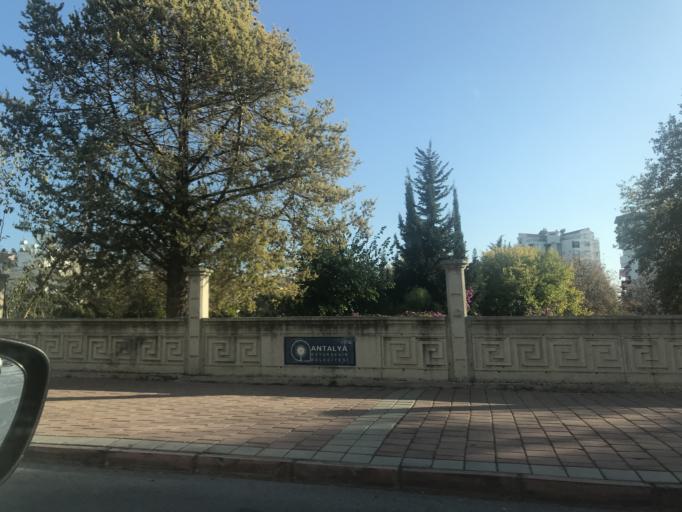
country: TR
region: Antalya
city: Antalya
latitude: 36.8530
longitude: 30.7729
